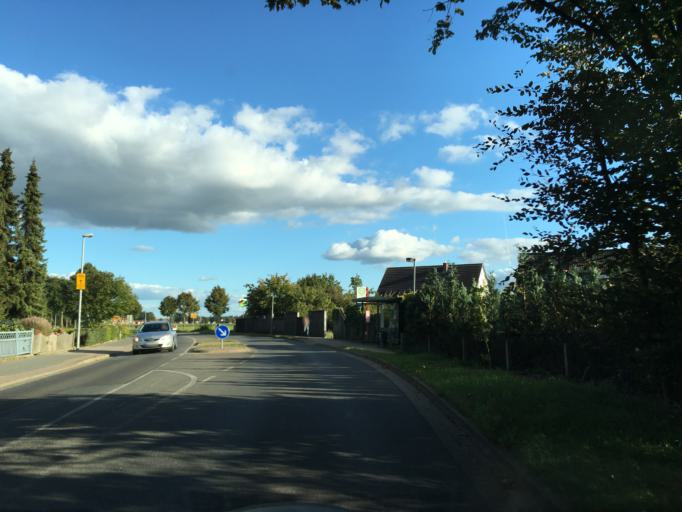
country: DE
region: Lower Saxony
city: Reppenstedt
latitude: 53.2469
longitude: 10.3677
